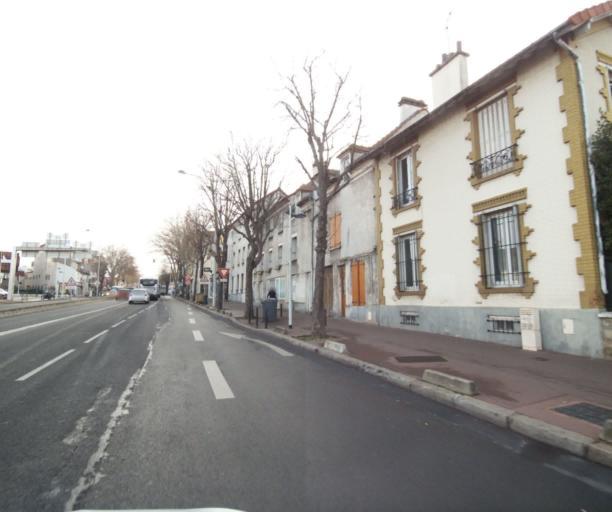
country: FR
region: Ile-de-France
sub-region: Departement des Hauts-de-Seine
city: Nanterre
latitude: 48.8868
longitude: 2.2039
